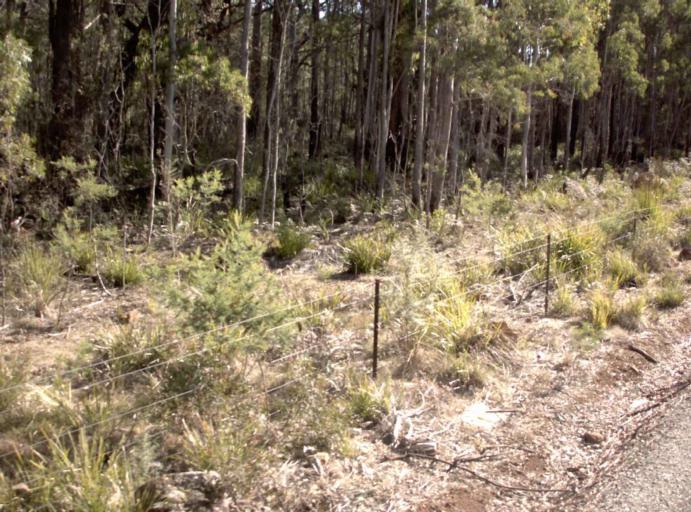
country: AU
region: Tasmania
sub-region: Launceston
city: Mayfield
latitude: -41.3181
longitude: 147.2086
